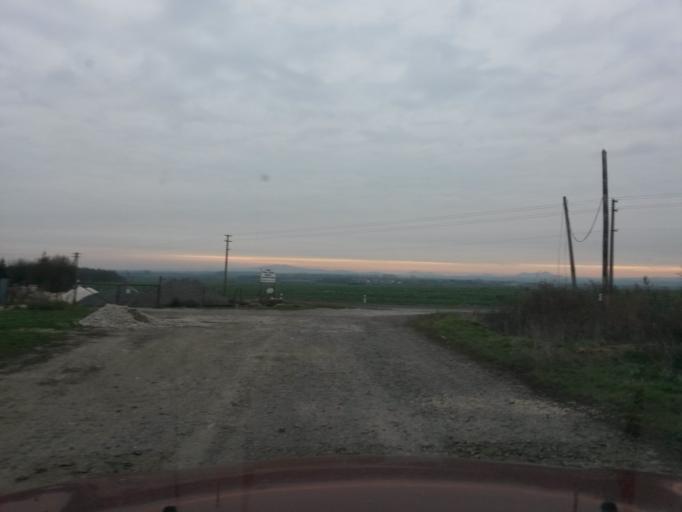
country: SK
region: Kosicky
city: Secovce
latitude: 48.6575
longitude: 21.6692
